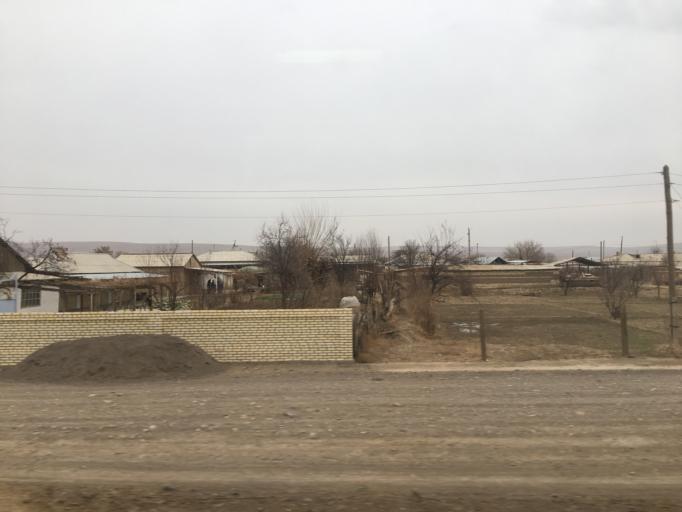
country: TM
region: Mary
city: Yoloeten
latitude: 36.5355
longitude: 62.5541
